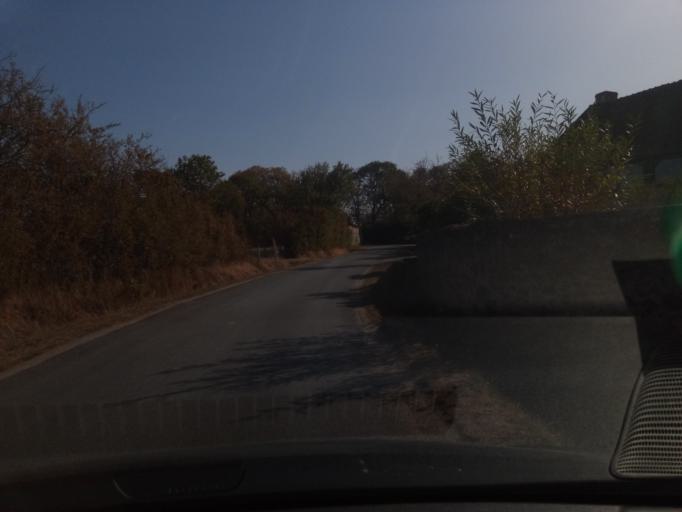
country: FR
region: Centre
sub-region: Departement de l'Indre
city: Mezieres-en-Brenne
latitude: 46.7209
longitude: 1.1738
